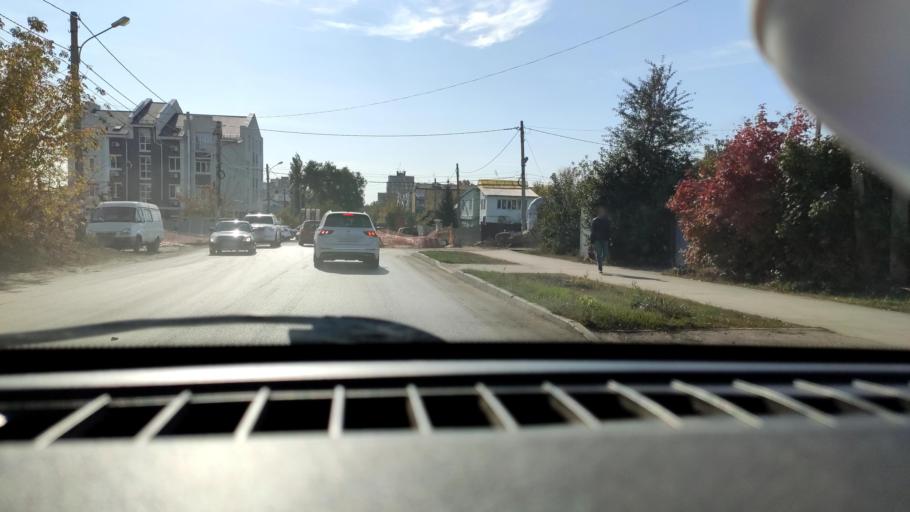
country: RU
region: Samara
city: Samara
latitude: 53.2048
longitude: 50.2034
